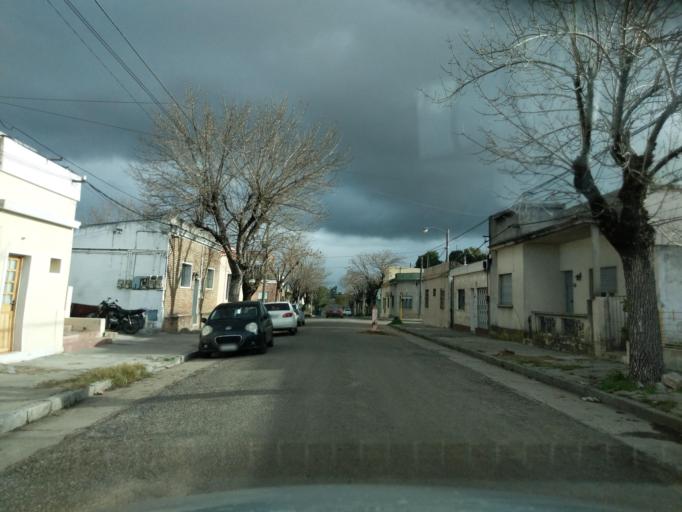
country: UY
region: Florida
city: Florida
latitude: -34.1020
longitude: -56.2181
